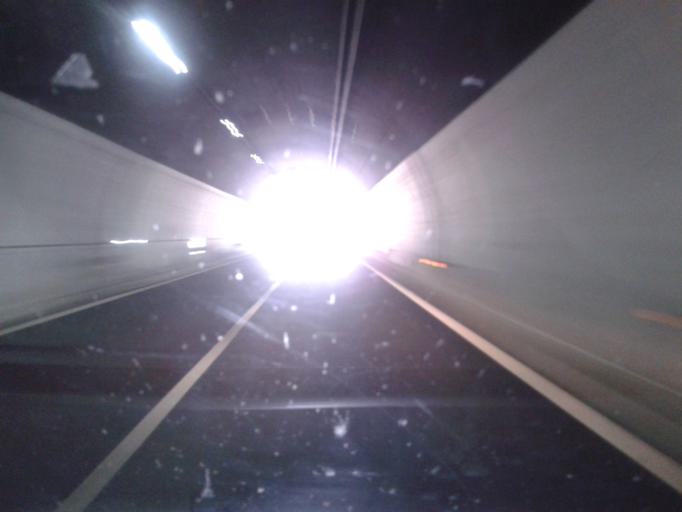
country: IT
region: Friuli Venezia Giulia
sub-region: Provincia di Udine
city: Dogna
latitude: 46.4425
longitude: 13.3090
